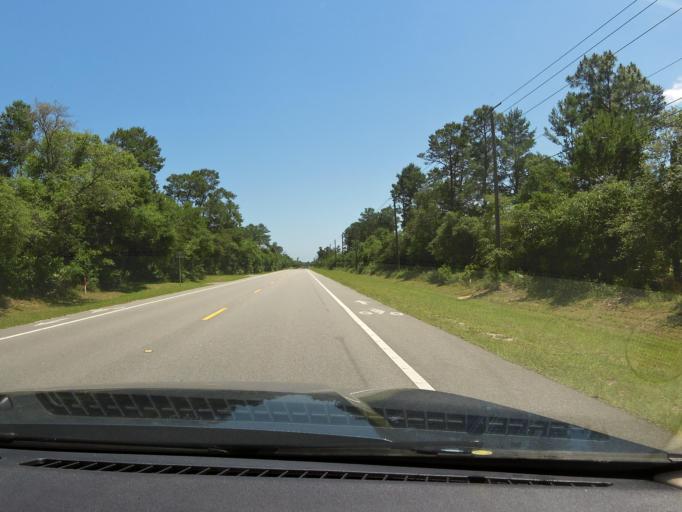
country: US
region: Florida
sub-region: Flagler County
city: Flagler Beach
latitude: 29.4437
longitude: -81.1614
